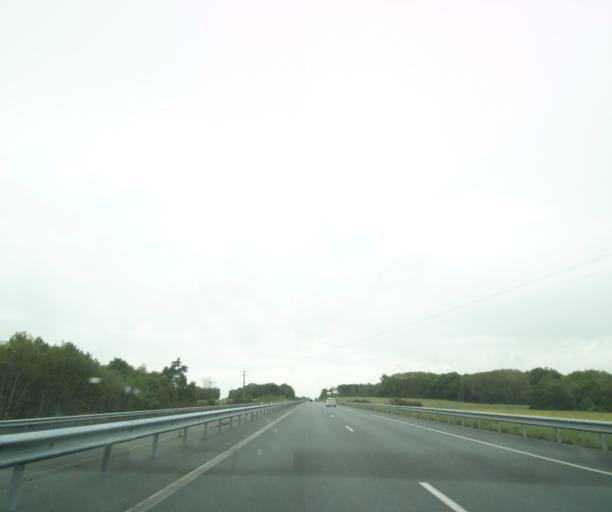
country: FR
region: Poitou-Charentes
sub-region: Departement de la Charente-Maritime
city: Chermignac
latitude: 45.7044
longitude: -0.7206
